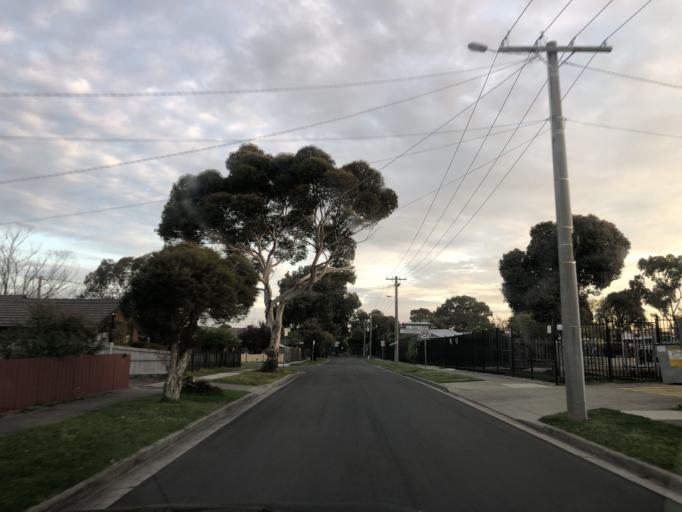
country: AU
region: Victoria
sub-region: Casey
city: Hampton Park
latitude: -38.0331
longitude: 145.2621
